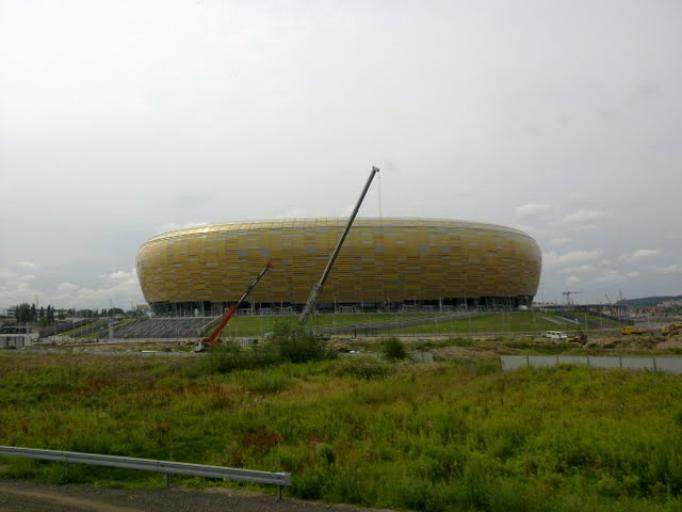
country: PL
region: Pomeranian Voivodeship
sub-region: Gdansk
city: Gdansk
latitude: 54.3930
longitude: 18.6415
